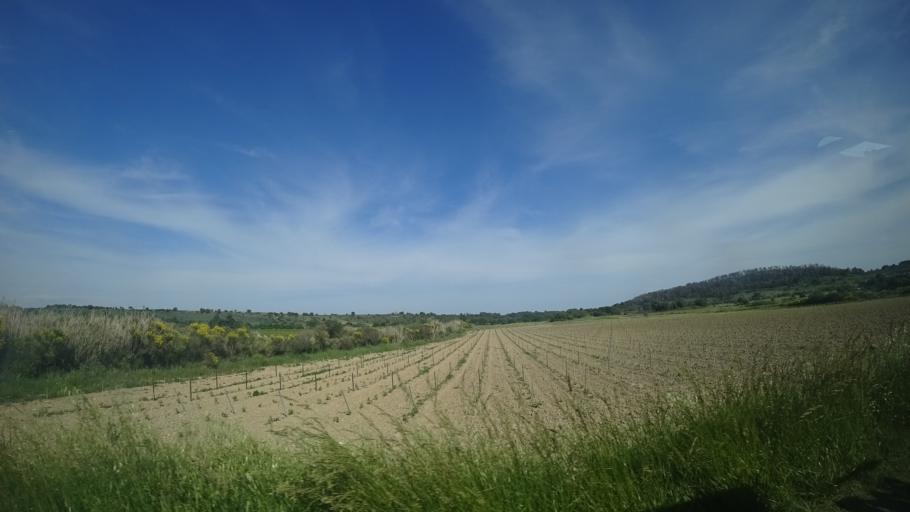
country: FR
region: Languedoc-Roussillon
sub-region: Departement de l'Aude
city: Canet
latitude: 43.2712
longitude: 2.8144
